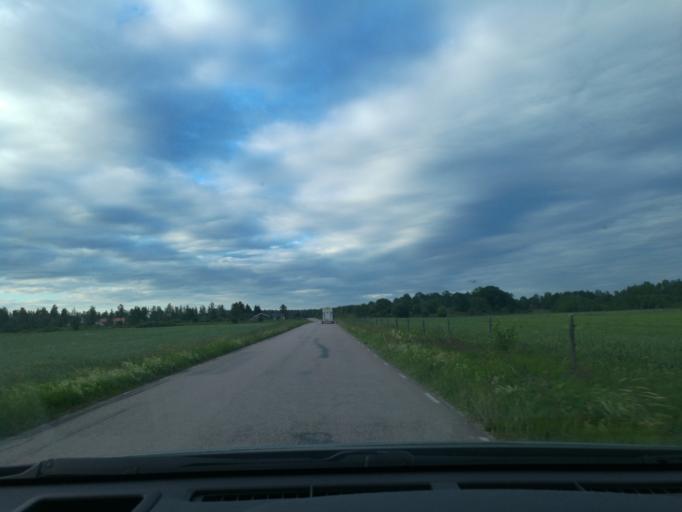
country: SE
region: Vaestmanland
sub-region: Hallstahammars Kommun
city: Kolback
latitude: 59.5396
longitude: 16.3043
